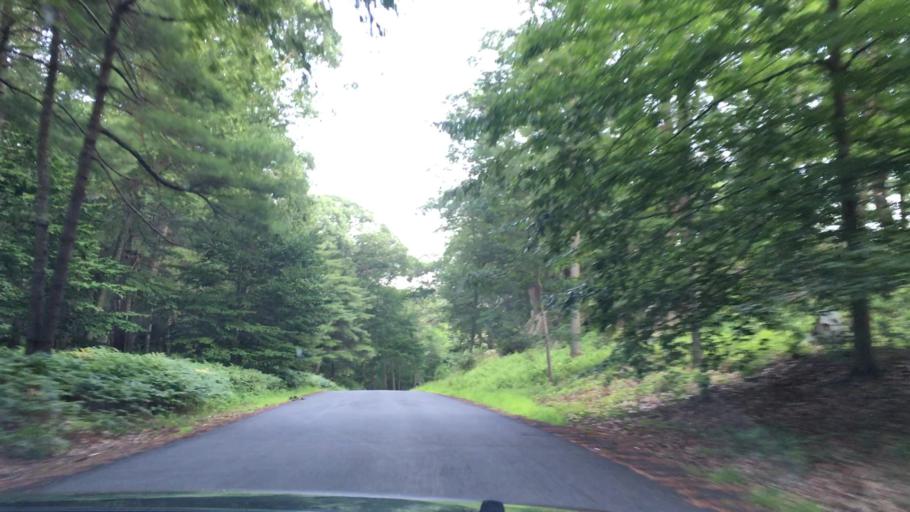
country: US
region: Massachusetts
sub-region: Essex County
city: Gloucester
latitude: 42.5789
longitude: -70.7273
